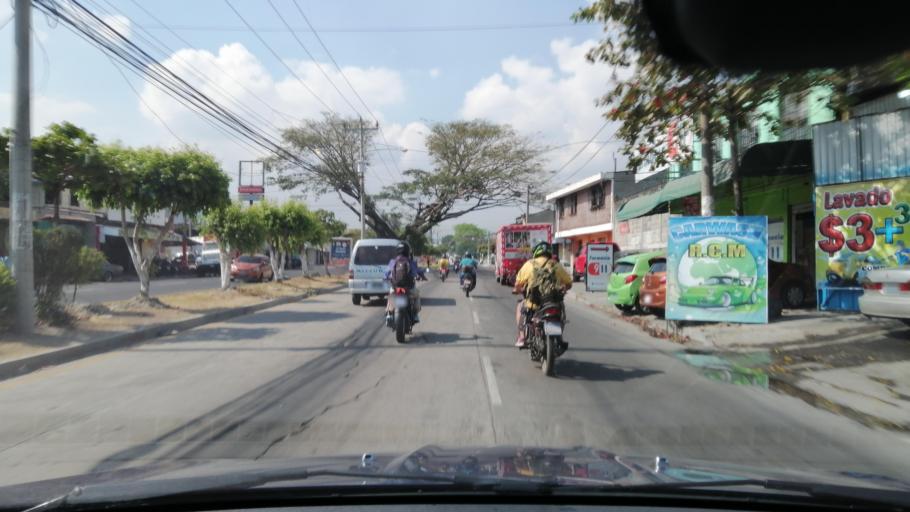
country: SV
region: San Salvador
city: Mejicanos
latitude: 13.7288
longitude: -89.2200
